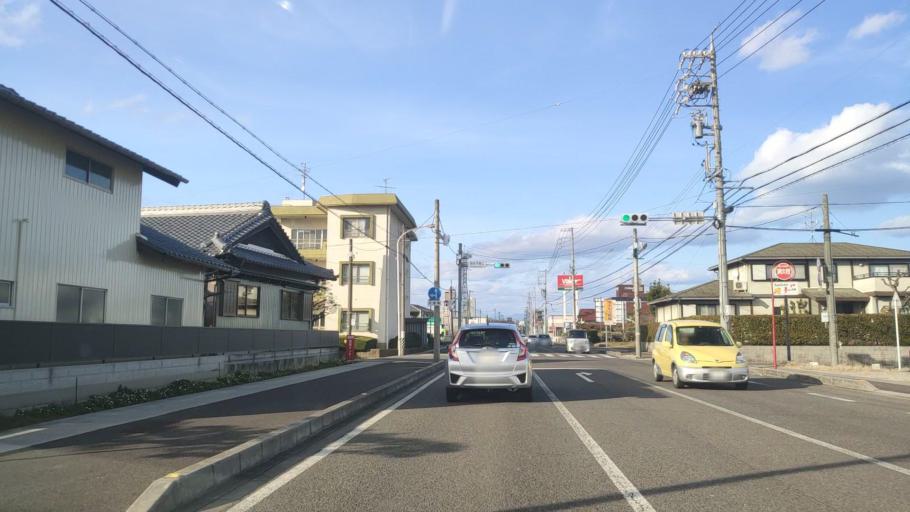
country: JP
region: Gifu
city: Kasamatsucho
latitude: 35.3897
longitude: 136.7546
